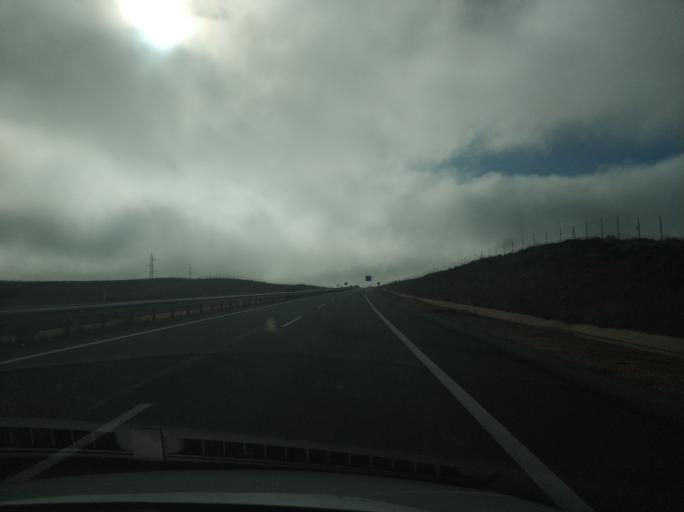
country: ES
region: Castille and Leon
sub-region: Provincia de Soria
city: Alcubilla de las Penas
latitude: 41.2757
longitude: -2.4749
